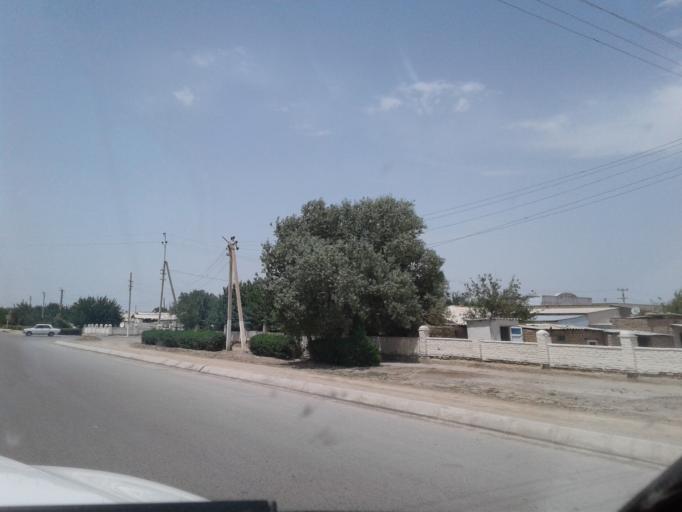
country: TM
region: Ahal
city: Tejen
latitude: 37.3715
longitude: 60.4897
